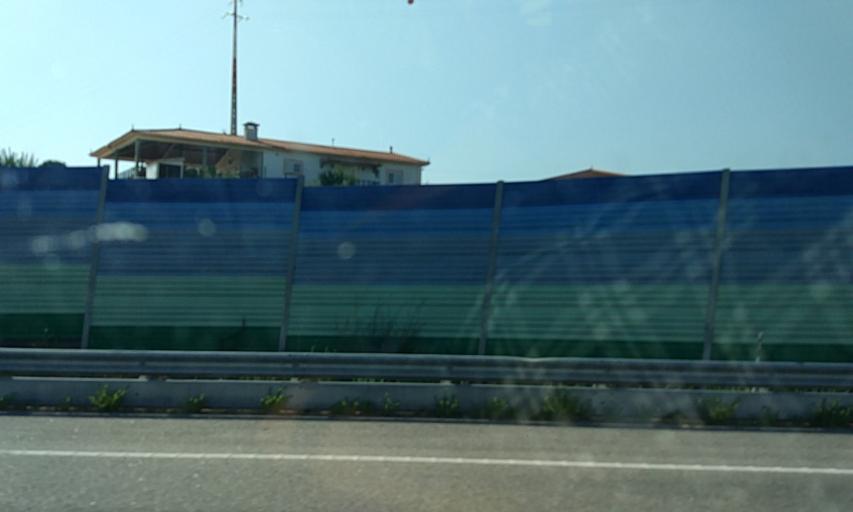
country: PT
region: Braganca
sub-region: Mirandela
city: Mirandela
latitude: 41.5138
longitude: -7.1782
